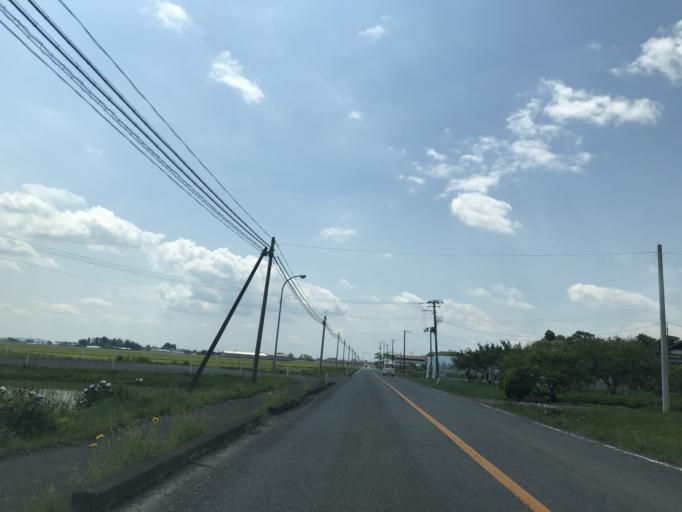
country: JP
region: Miyagi
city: Kogota
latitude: 38.6166
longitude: 141.0194
